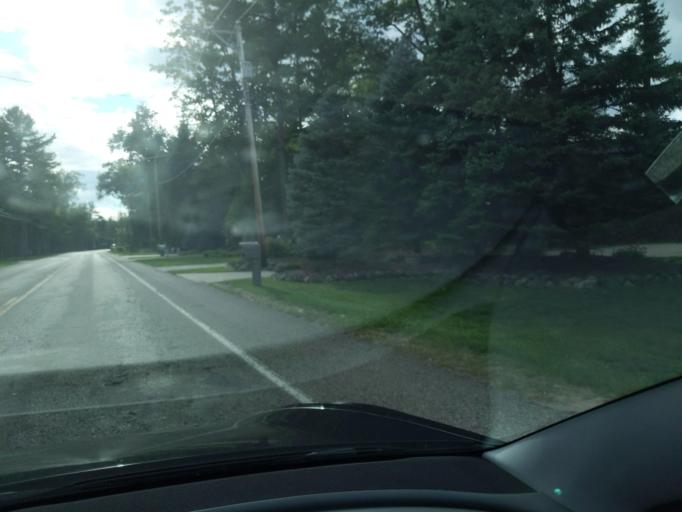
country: US
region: Michigan
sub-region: Kalkaska County
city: Rapid City
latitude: 44.8547
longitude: -85.3061
